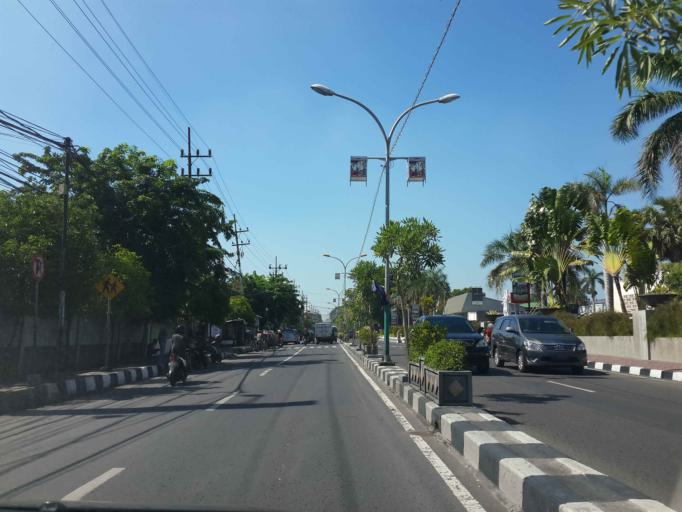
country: ID
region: East Java
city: Kebomas
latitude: -7.1763
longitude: 112.6515
